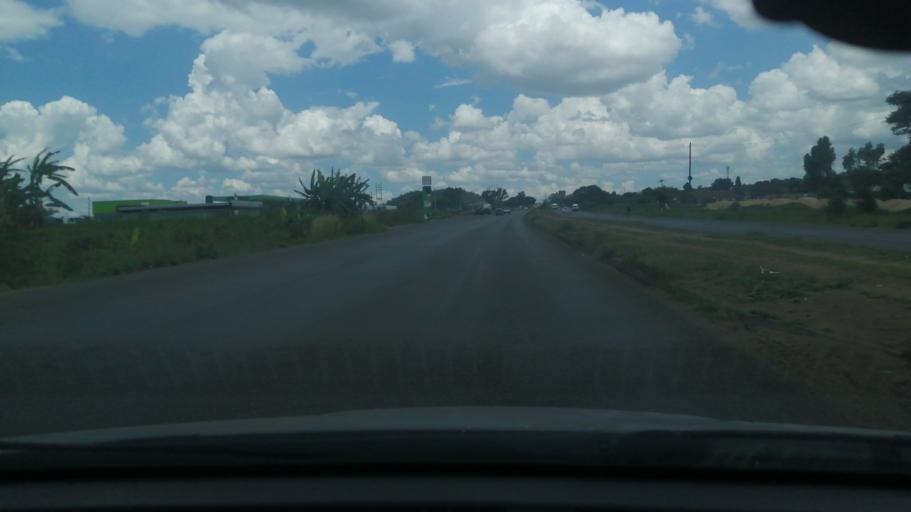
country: ZW
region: Harare
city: Harare
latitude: -17.8222
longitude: 30.9648
